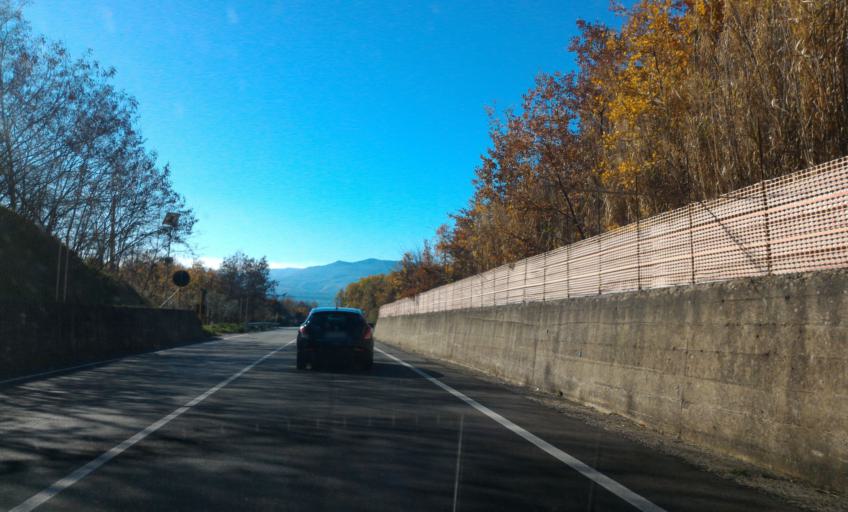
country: IT
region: Calabria
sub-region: Provincia di Cosenza
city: Rovito
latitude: 39.3086
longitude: 16.3252
